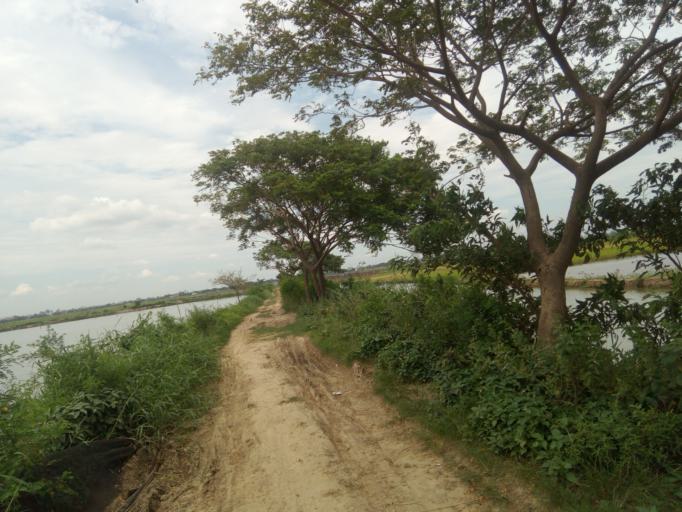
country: BD
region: Dhaka
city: Paltan
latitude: 23.7251
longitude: 90.4610
